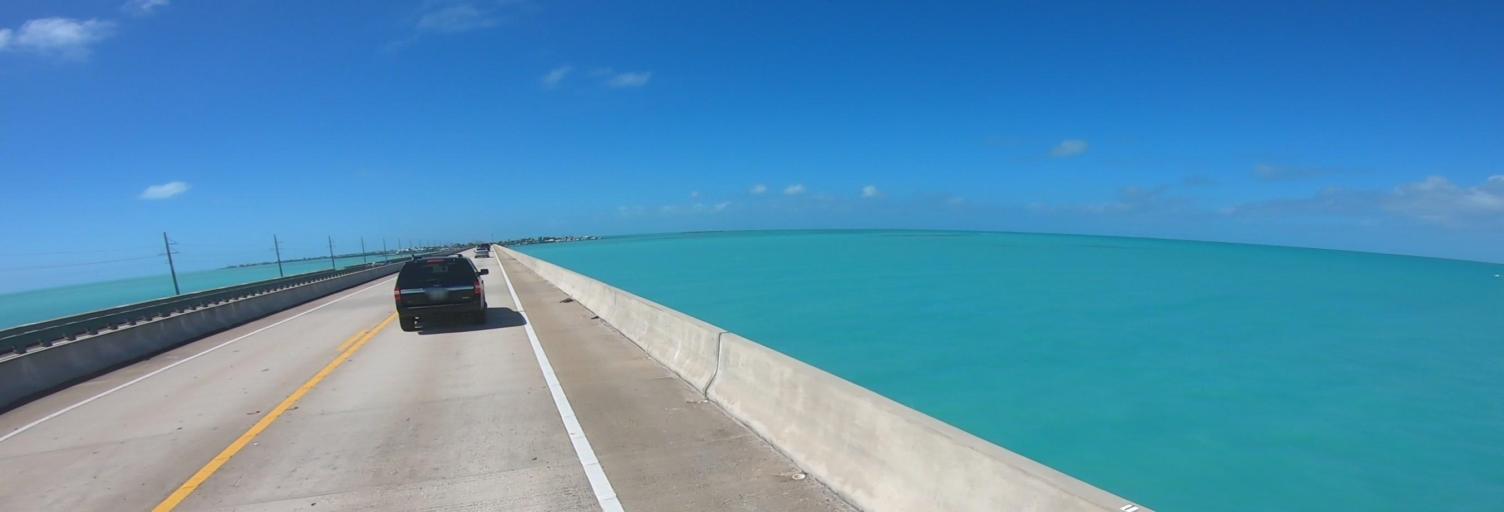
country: US
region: Florida
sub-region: Monroe County
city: Marathon
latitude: 24.7950
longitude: -80.8741
